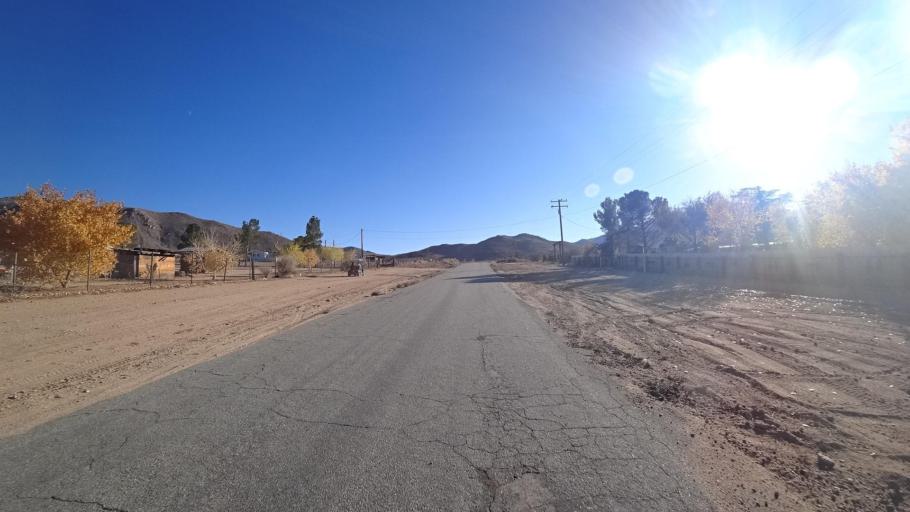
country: US
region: California
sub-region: Kern County
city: Weldon
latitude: 35.5436
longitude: -118.2069
